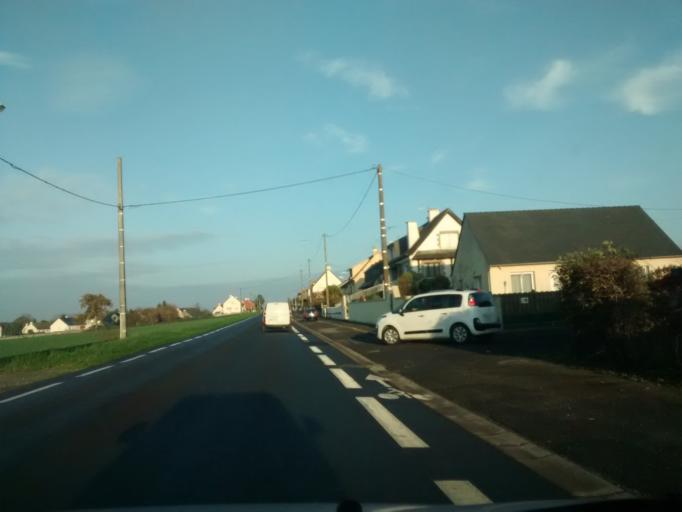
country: FR
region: Lower Normandy
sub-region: Departement de la Manche
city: Pontorson
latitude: 48.5422
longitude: -1.4964
